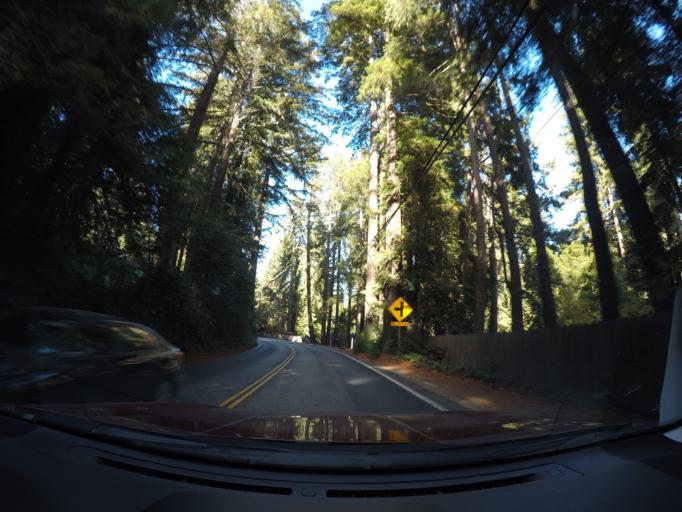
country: US
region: California
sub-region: Santa Cruz County
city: Brookdale
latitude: 37.1123
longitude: -122.1149
